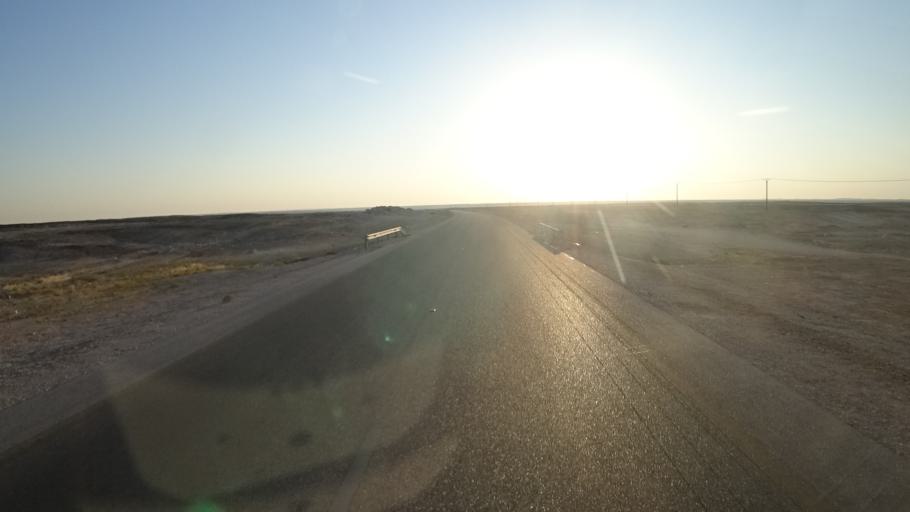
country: OM
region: Zufar
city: Salalah
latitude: 17.5381
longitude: 53.4117
